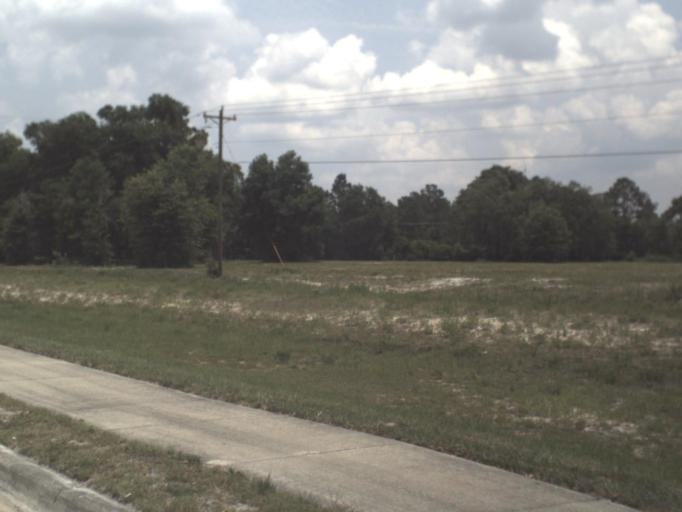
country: US
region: Florida
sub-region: Putnam County
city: Palatka
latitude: 29.6353
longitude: -81.6809
